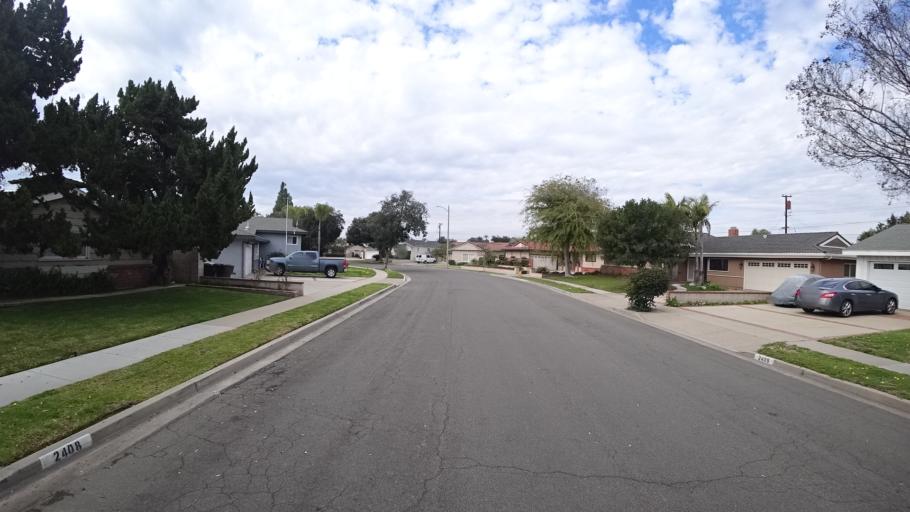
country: US
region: California
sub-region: Orange County
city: Placentia
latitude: 33.8428
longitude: -117.8824
